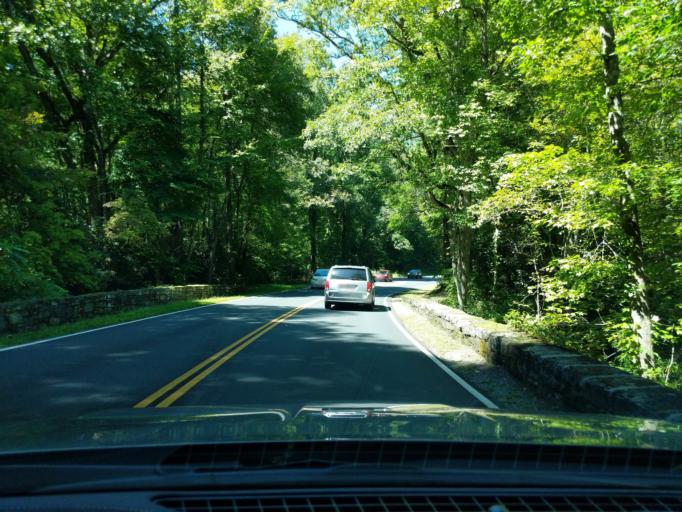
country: US
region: North Carolina
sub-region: Swain County
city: Cherokee
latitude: 35.5201
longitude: -83.3078
